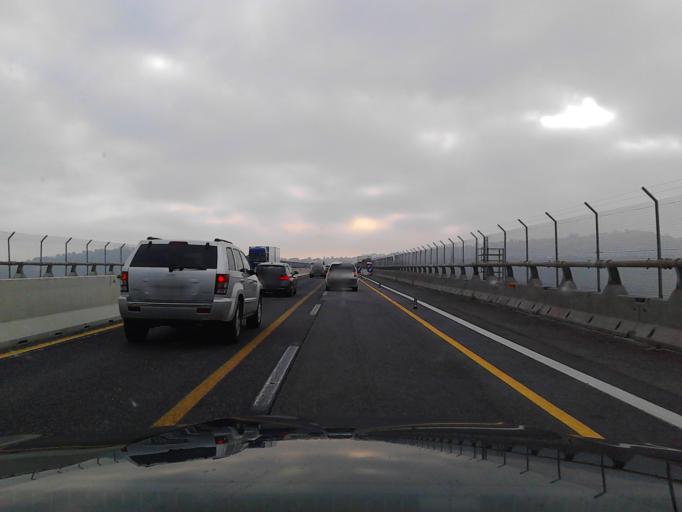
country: IT
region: Abruzzo
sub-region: Provincia di Teramo
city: Tortoreto Lido
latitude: 42.7823
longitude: 13.9344
